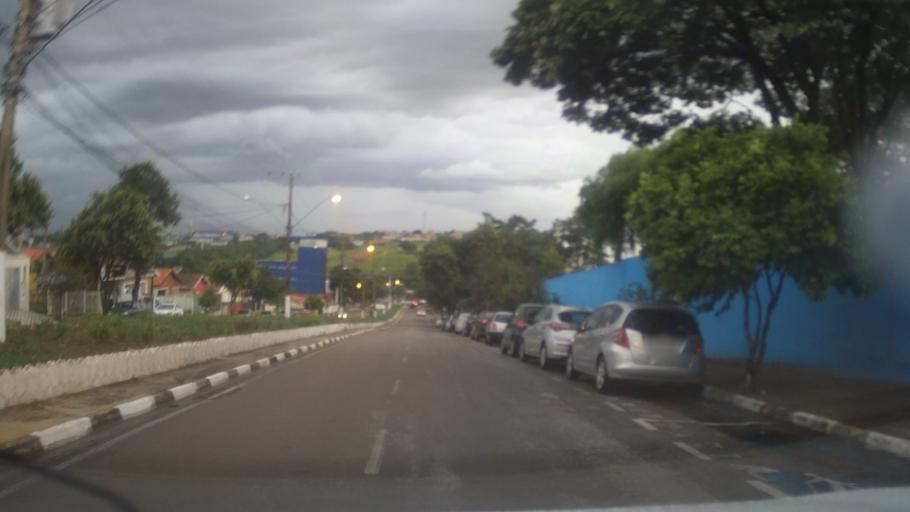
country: BR
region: Sao Paulo
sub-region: Itupeva
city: Itupeva
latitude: -23.1597
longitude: -47.0594
